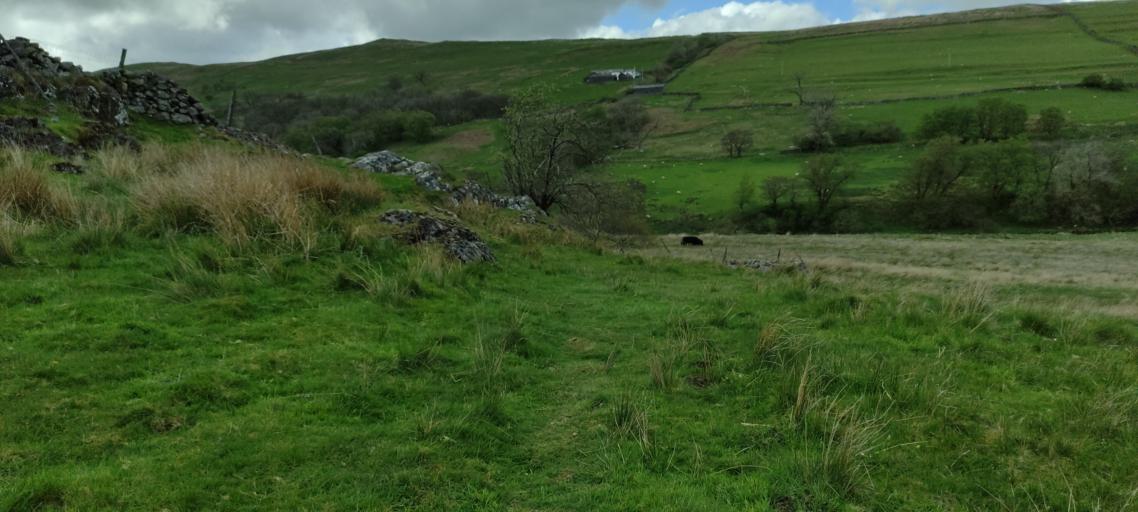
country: GB
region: England
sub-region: Cumbria
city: Kendal
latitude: 54.4932
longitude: -2.7048
